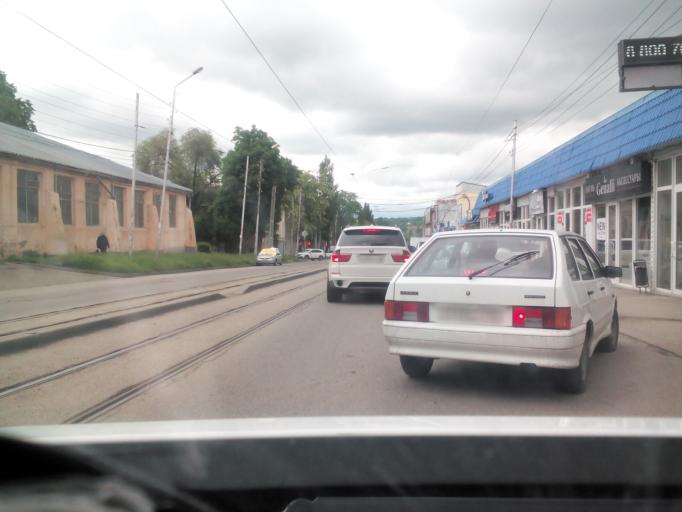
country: RU
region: Stavropol'skiy
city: Pyatigorsk
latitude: 44.0430
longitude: 43.0641
